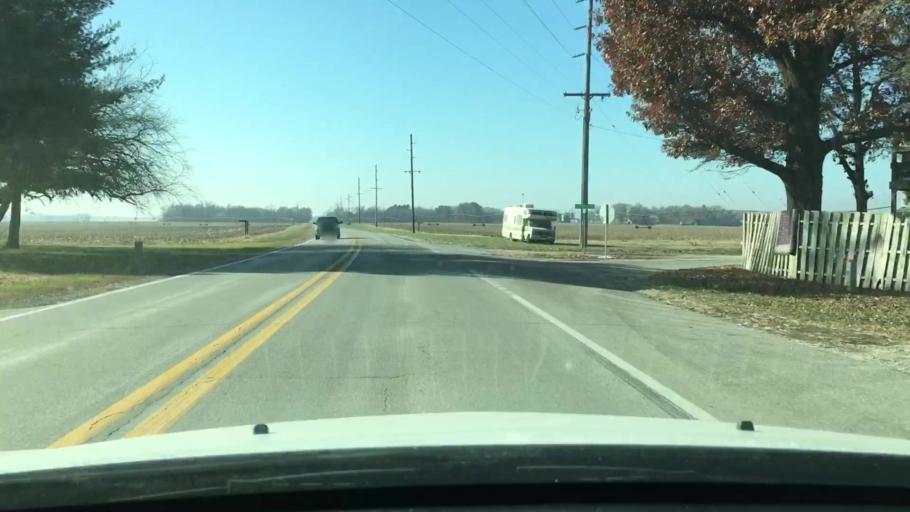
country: US
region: Illinois
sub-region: Cass County
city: Beardstown
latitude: 39.9777
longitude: -90.4559
